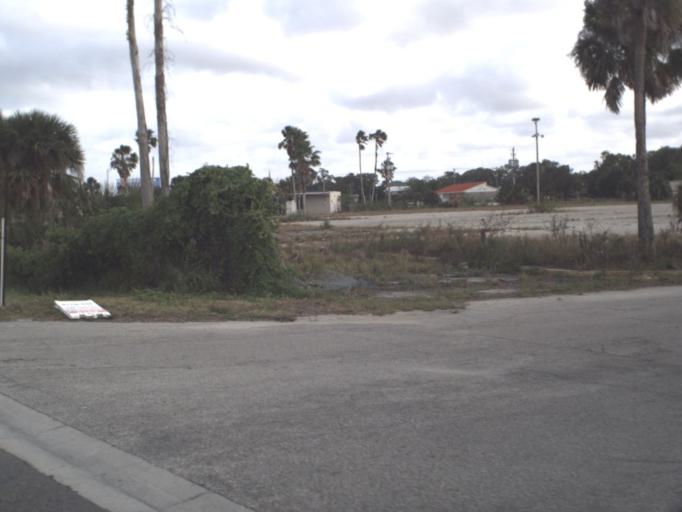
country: US
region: Florida
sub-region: Brevard County
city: Titusville
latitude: 28.6183
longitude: -80.8081
